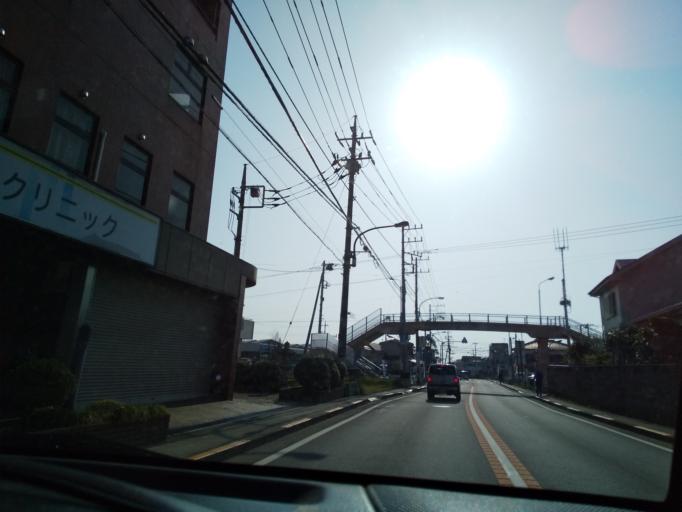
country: JP
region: Tokyo
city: Fussa
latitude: 35.7289
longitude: 139.3104
